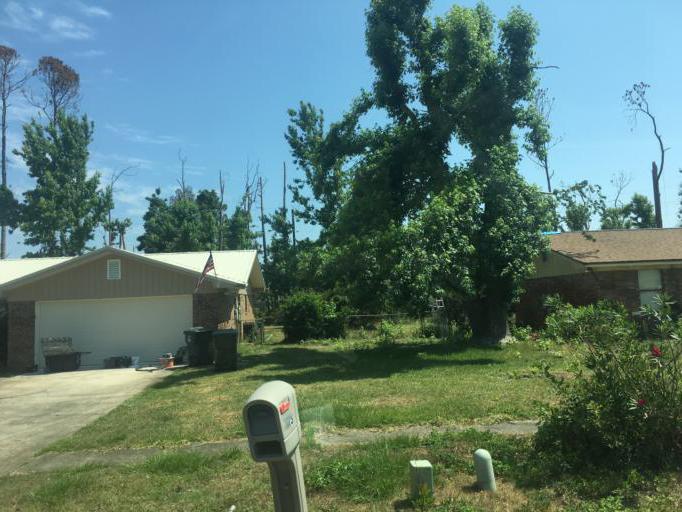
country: US
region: Florida
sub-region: Bay County
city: Lynn Haven
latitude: 30.2227
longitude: -85.6551
